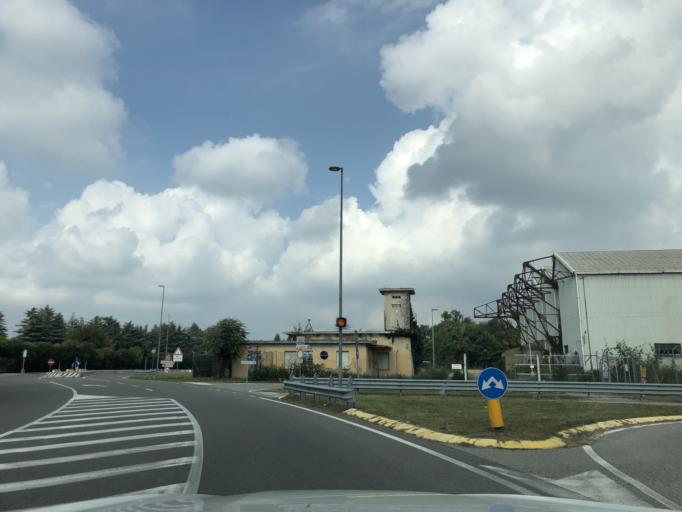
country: IT
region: Lombardy
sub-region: Provincia di Varese
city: Vizzola Ticino
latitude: 45.6407
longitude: 8.7139
